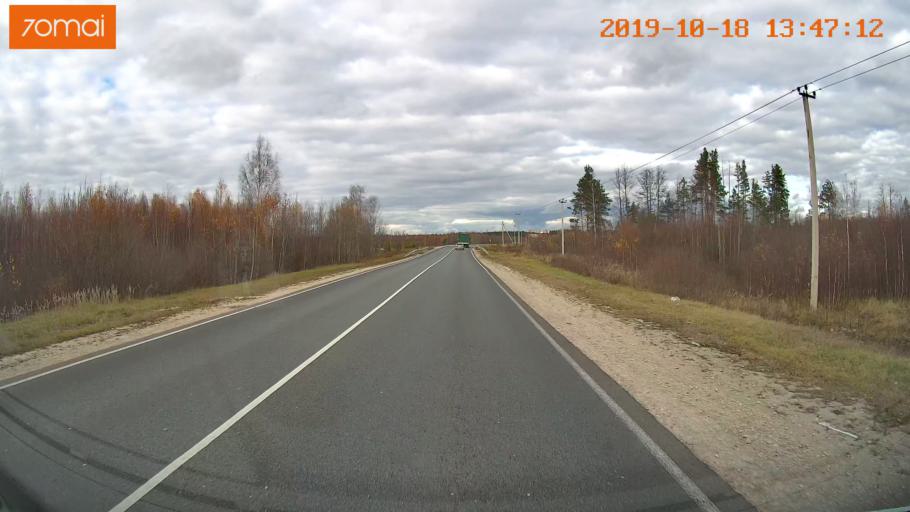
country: RU
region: Rjazan
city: Solotcha
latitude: 54.9711
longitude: 39.9514
